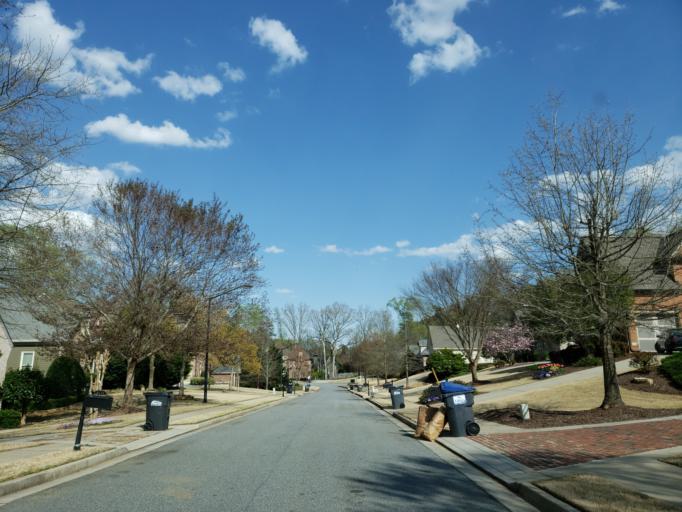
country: US
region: Georgia
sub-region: Cherokee County
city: Woodstock
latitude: 34.0310
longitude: -84.4792
